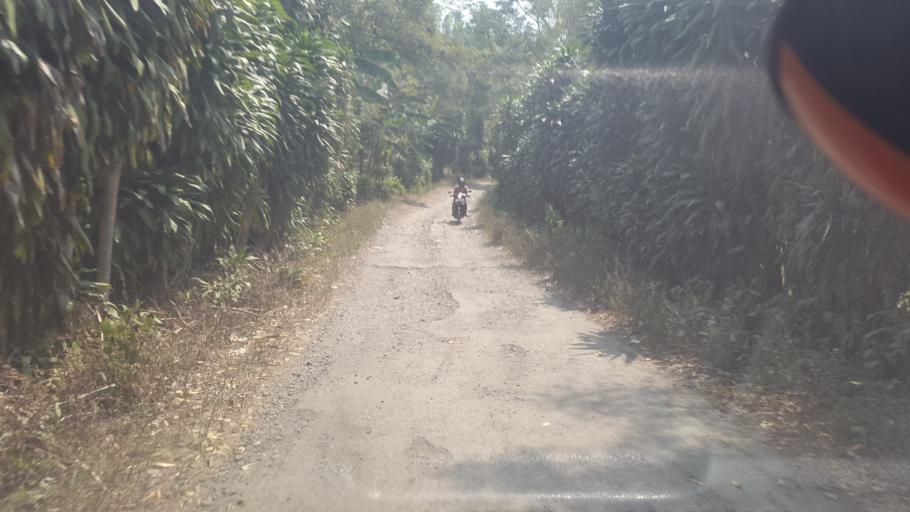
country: ID
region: West Java
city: Nagrak
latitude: -6.8959
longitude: 106.5245
